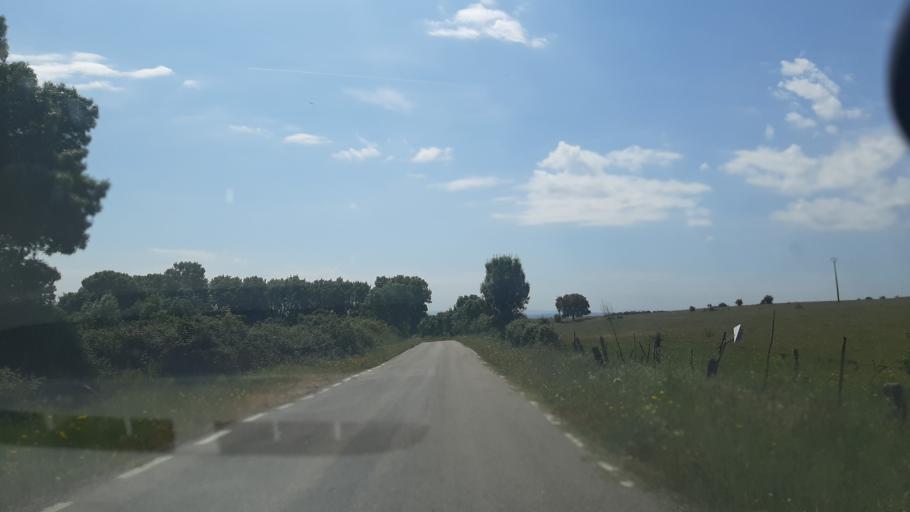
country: ES
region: Castille and Leon
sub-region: Provincia de Salamanca
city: Gallegos de Arganan
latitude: 40.6404
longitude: -6.7306
